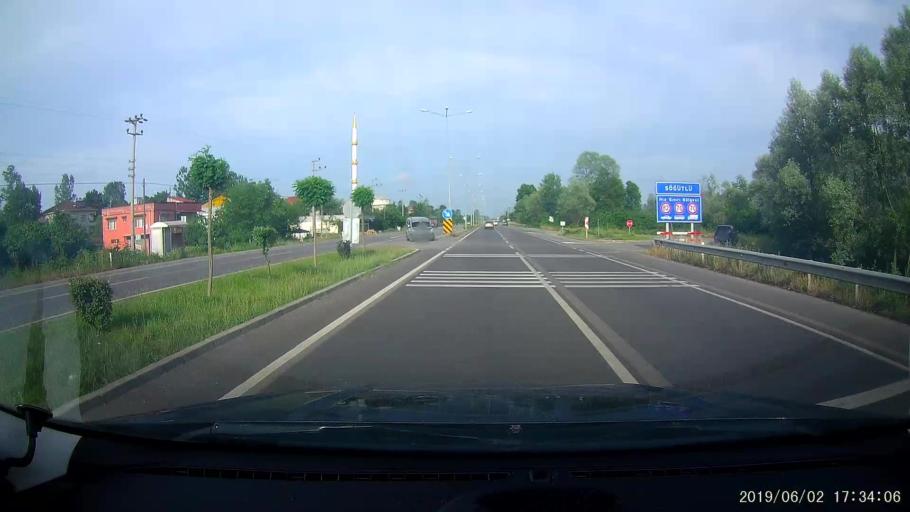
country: TR
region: Samsun
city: Terme
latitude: 41.2205
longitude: 36.8622
